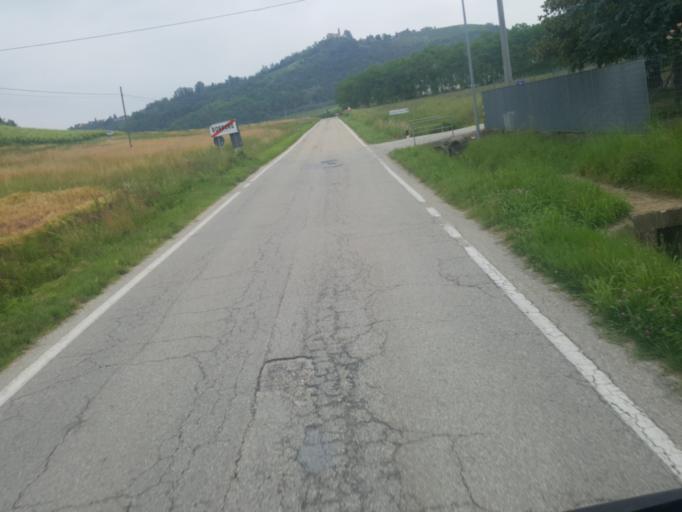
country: IT
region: Piedmont
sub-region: Provincia di Cuneo
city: Vezza d'Alba
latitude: 44.7627
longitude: 8.0166
